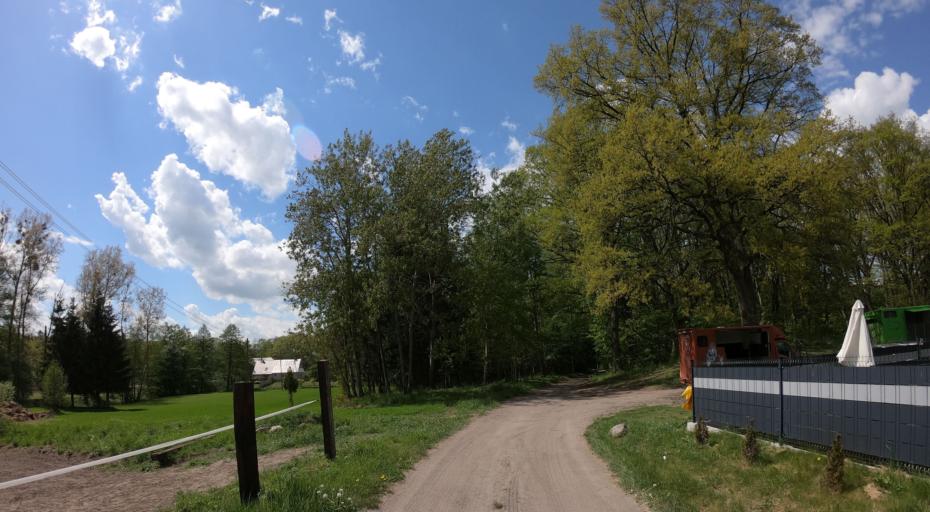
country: PL
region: West Pomeranian Voivodeship
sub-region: Powiat lobeski
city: Lobez
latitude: 53.6026
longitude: 15.6576
